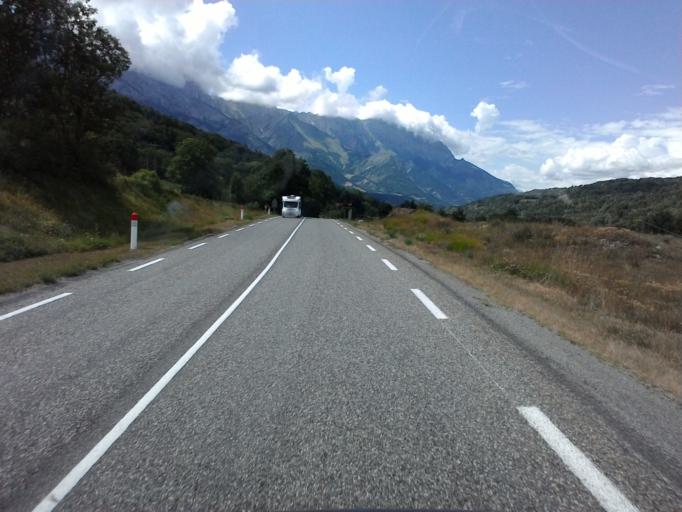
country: FR
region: Provence-Alpes-Cote d'Azur
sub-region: Departement des Hautes-Alpes
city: Saint-Bonnet-en-Champsaur
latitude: 44.7048
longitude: 6.0444
